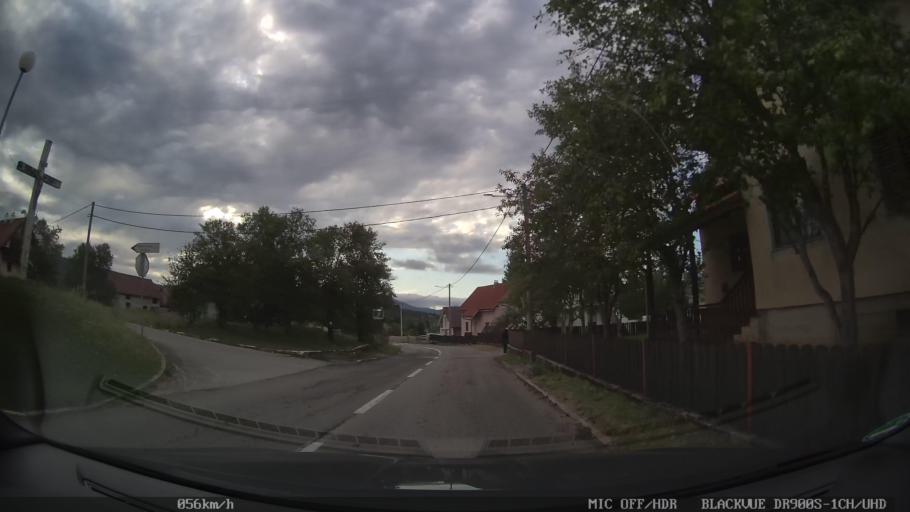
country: HR
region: Karlovacka
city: Plaski
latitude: 44.9835
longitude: 15.4787
